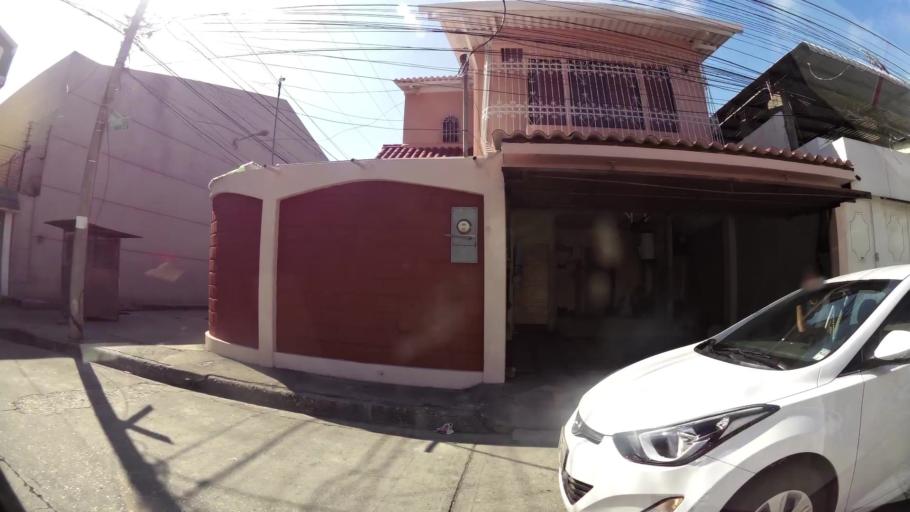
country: EC
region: Guayas
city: Guayaquil
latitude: -2.2288
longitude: -79.8968
